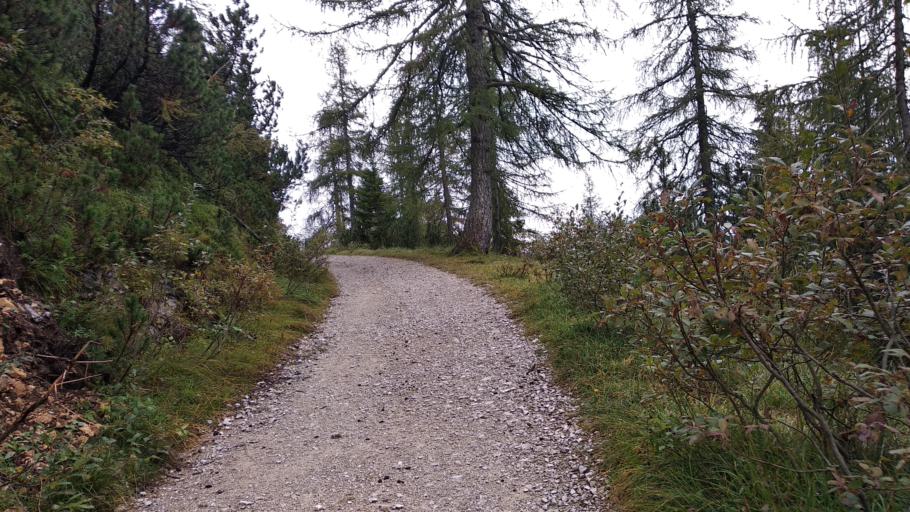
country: IT
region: Trentino-Alto Adige
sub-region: Provincia di Trento
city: Borgo
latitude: 45.9692
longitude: 11.4367
